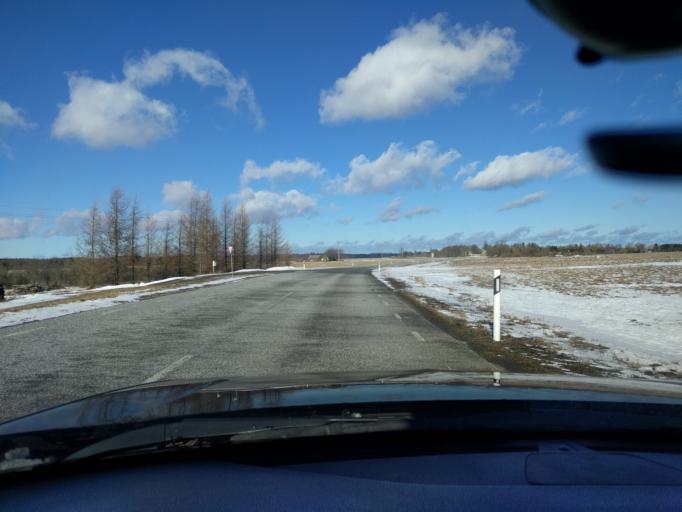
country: EE
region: Harju
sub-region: Raasiku vald
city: Raasiku
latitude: 59.3899
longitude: 25.1888
